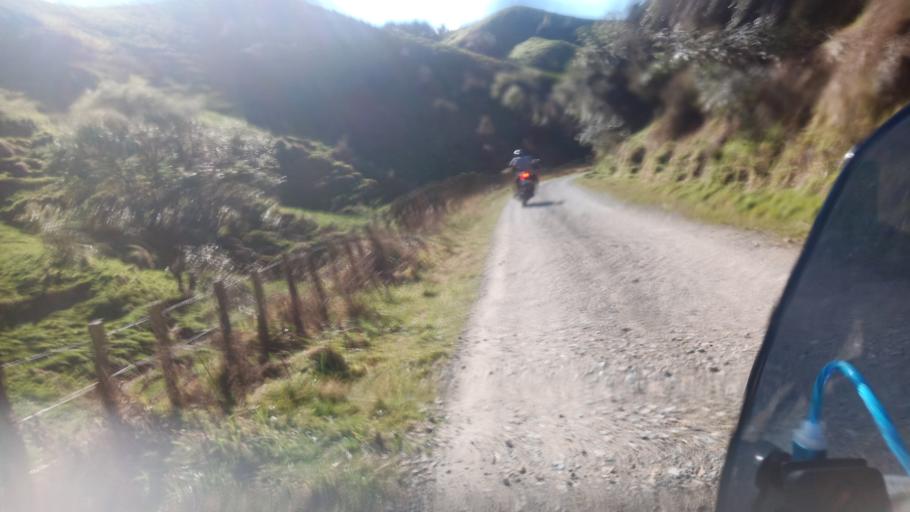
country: NZ
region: Hawke's Bay
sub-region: Wairoa District
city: Wairoa
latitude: -38.6627
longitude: 177.4864
